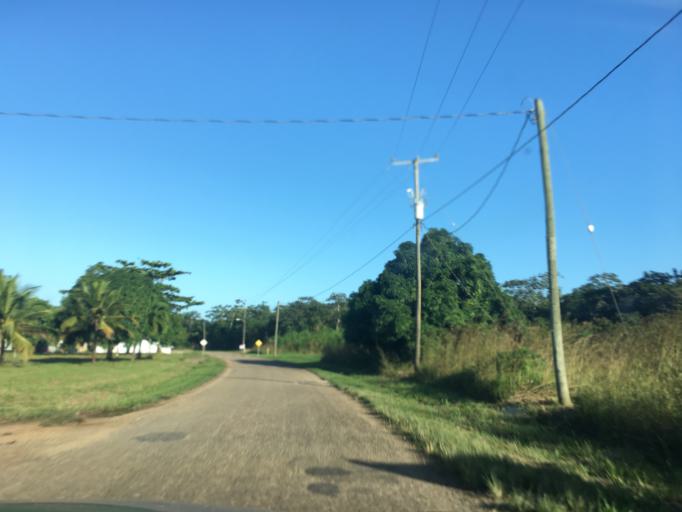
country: BZ
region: Stann Creek
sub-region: Dangriga
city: Dangriga
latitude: 16.8205
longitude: -88.3223
